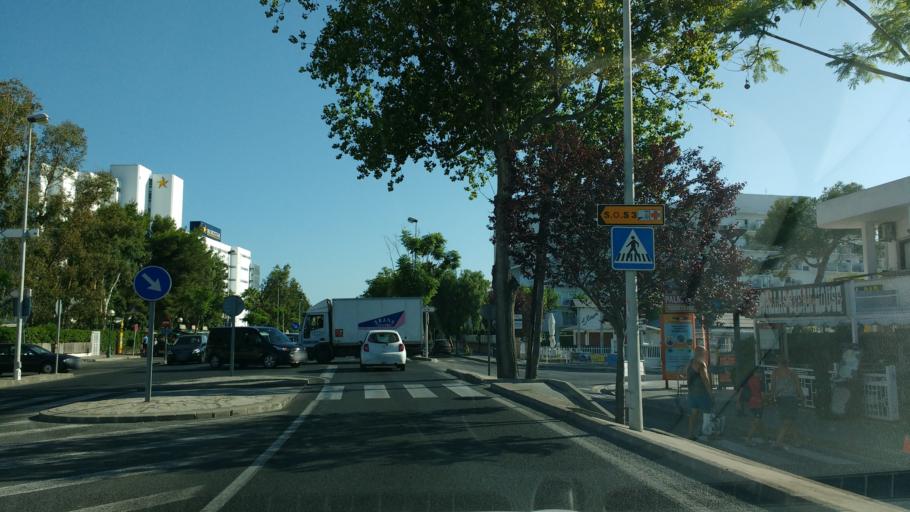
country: ES
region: Balearic Islands
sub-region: Illes Balears
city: Port d'Alcudia
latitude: 39.8340
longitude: 3.1177
